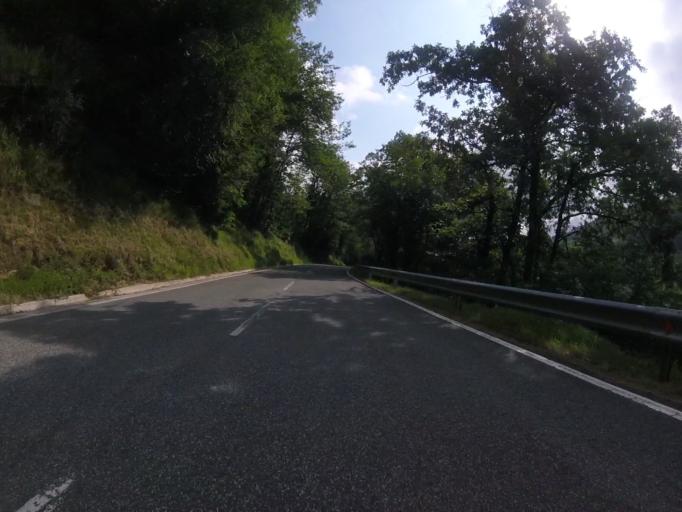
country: ES
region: Navarre
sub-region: Provincia de Navarra
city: Ezkurra
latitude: 43.0837
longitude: -1.8133
